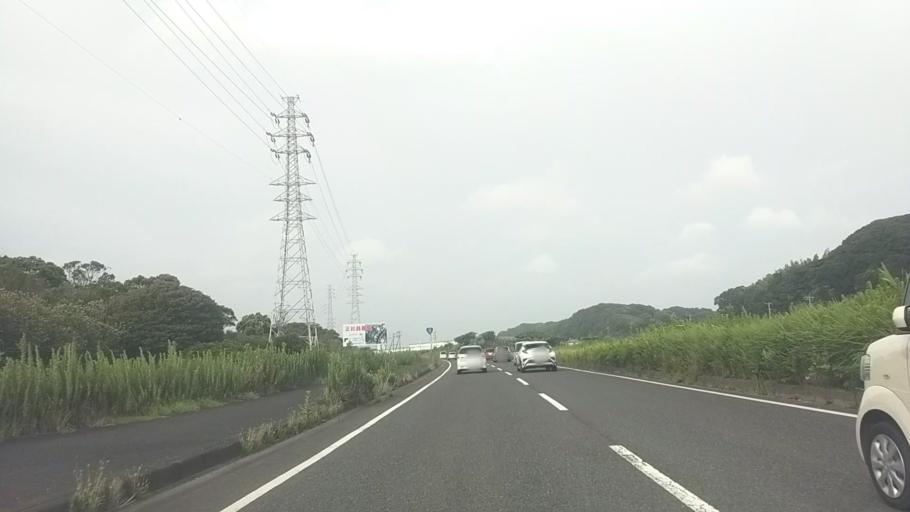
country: JP
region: Chiba
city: Kisarazu
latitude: 35.3535
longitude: 139.9037
